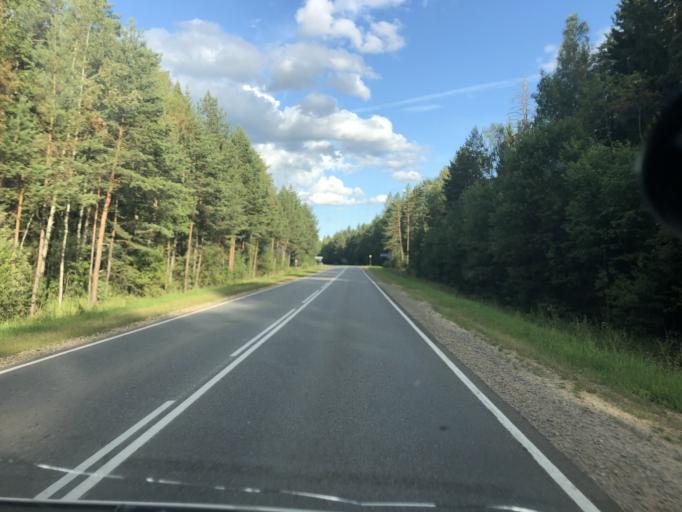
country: RU
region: Kaluga
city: Yukhnov
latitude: 54.7148
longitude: 35.2371
